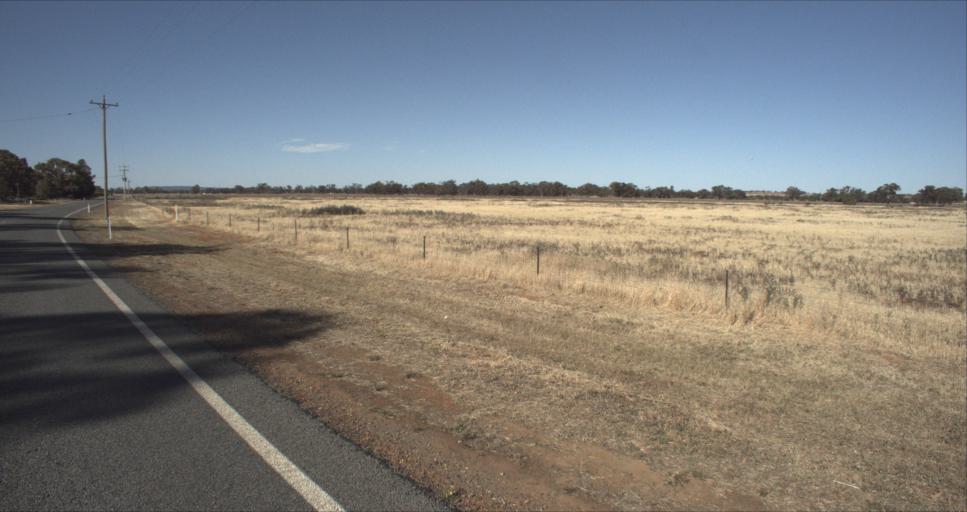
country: AU
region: New South Wales
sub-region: Leeton
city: Leeton
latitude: -34.6229
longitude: 146.3957
